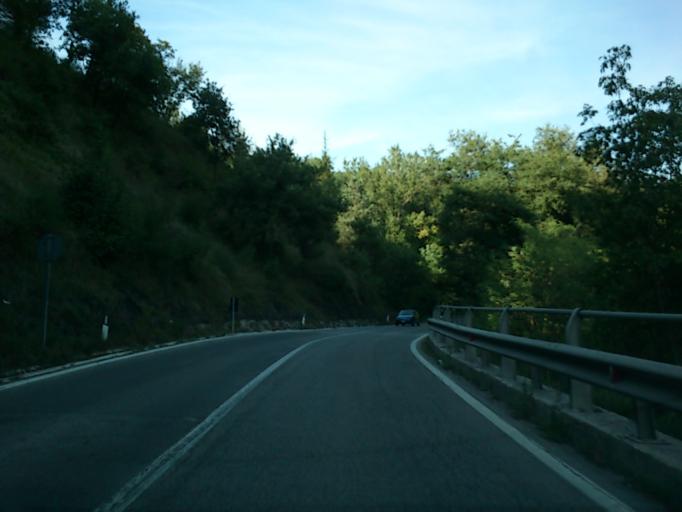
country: IT
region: The Marches
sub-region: Provincia di Pesaro e Urbino
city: Canavaccio
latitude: 43.6990
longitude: 12.6785
